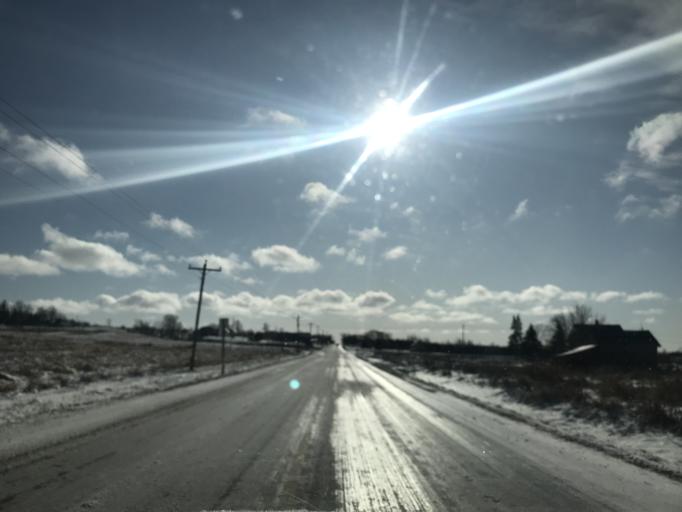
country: US
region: Wisconsin
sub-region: Kewaunee County
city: Luxemburg
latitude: 44.7139
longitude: -87.6207
